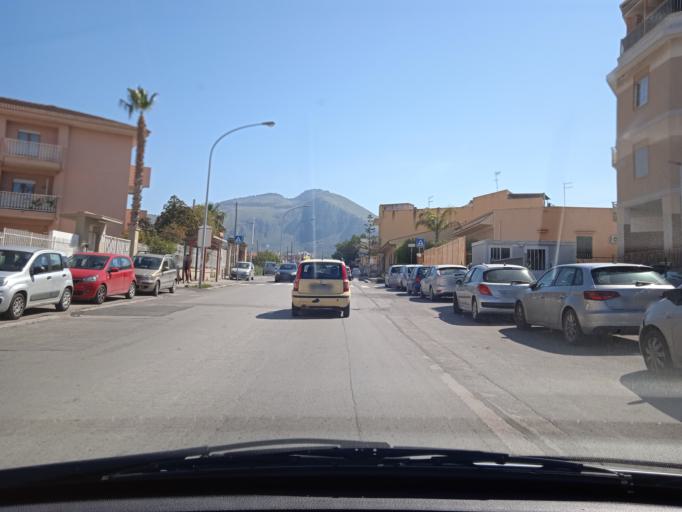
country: IT
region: Sicily
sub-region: Palermo
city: Villabate
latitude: 38.0890
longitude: 13.4327
